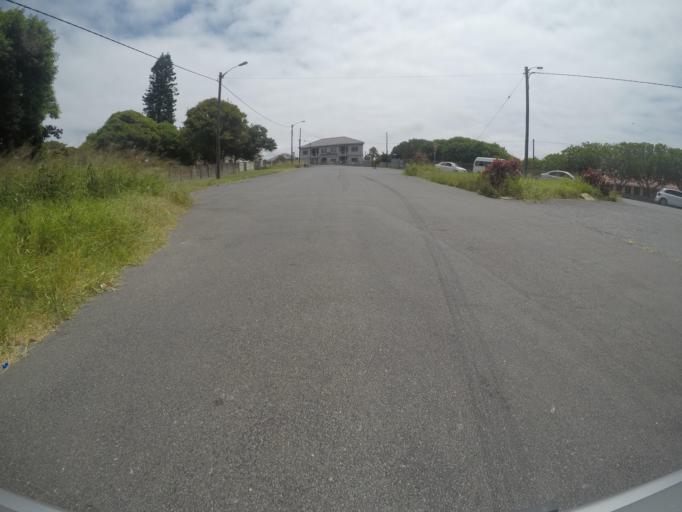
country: ZA
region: Eastern Cape
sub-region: Buffalo City Metropolitan Municipality
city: East London
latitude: -33.0215
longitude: 27.9124
